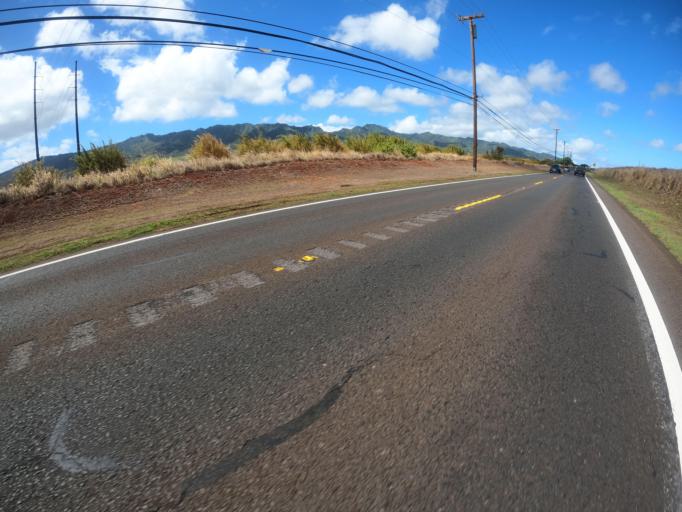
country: US
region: Hawaii
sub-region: Honolulu County
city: Village Park
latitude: 21.4142
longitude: -158.0462
